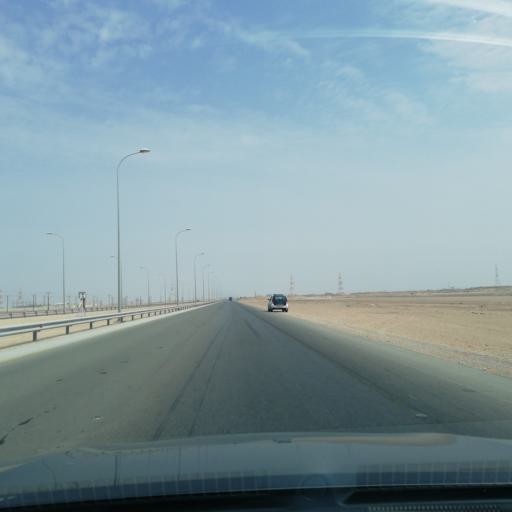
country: OM
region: Zufar
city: Salalah
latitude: 17.5816
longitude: 54.0427
